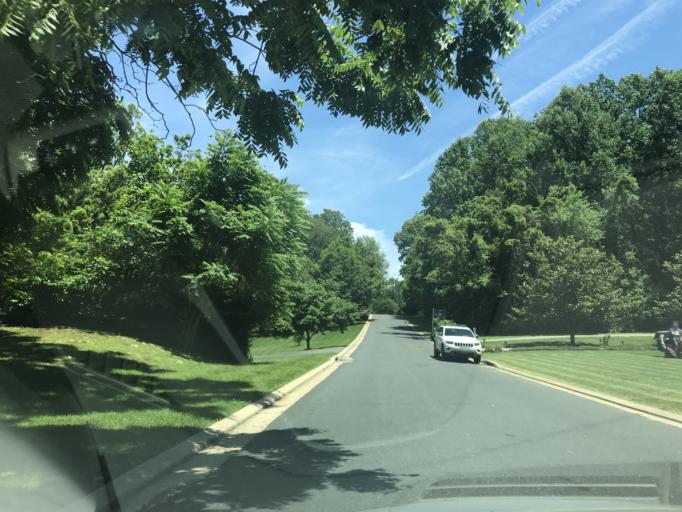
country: US
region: Maryland
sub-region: Baltimore County
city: Kingsville
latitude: 39.4705
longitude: -76.4536
